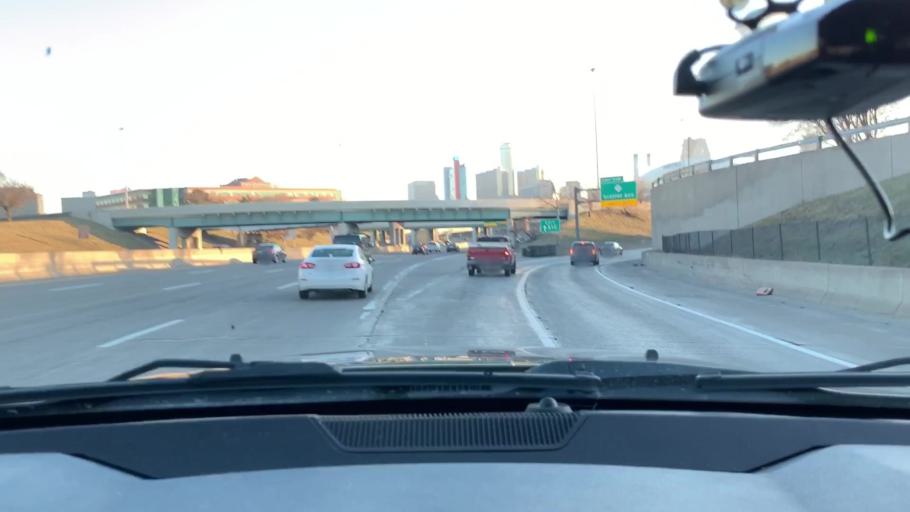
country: US
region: Michigan
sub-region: Wayne County
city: Detroit
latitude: 42.3459
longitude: -83.0447
